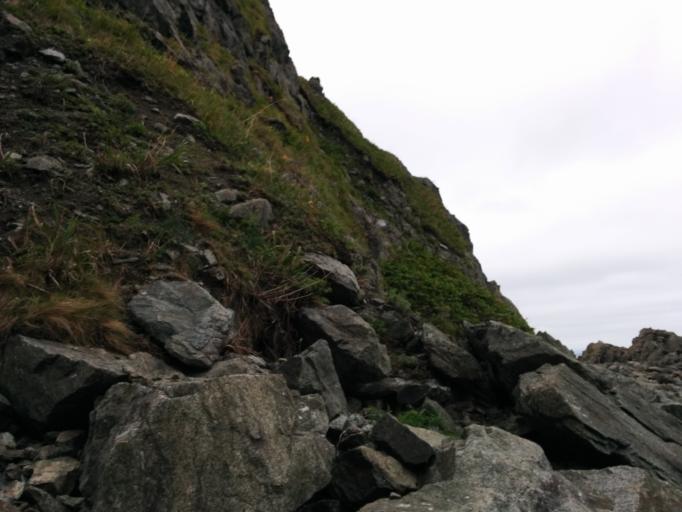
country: JP
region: Hokkaido
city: Iwanai
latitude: 42.3112
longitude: 139.7681
